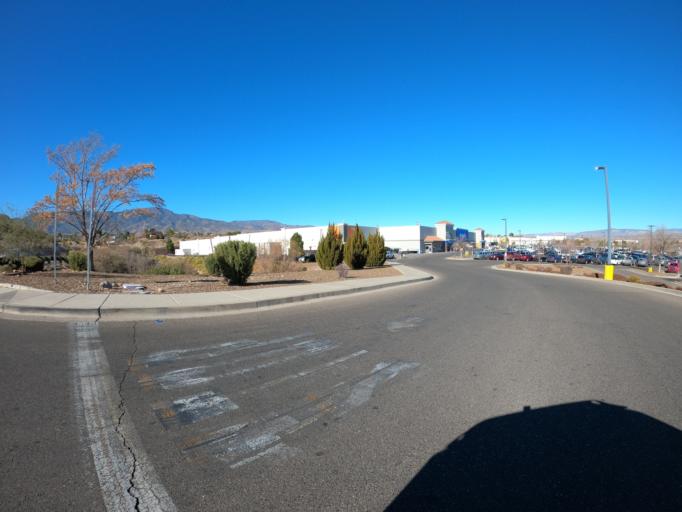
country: US
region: Arizona
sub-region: Yavapai County
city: Verde Village
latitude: 34.7121
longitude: -111.9999
